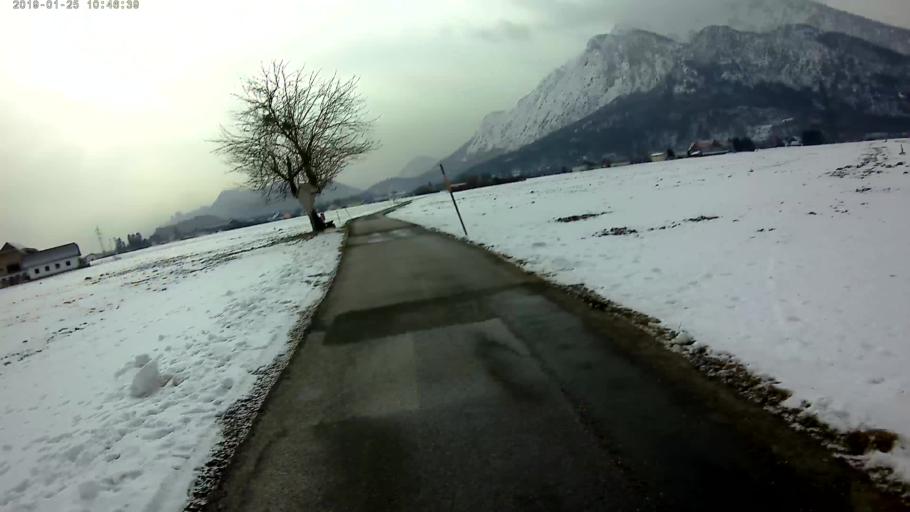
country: AT
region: Salzburg
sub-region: Politischer Bezirk Salzburg-Umgebung
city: Grodig
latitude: 47.7507
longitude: 13.0411
